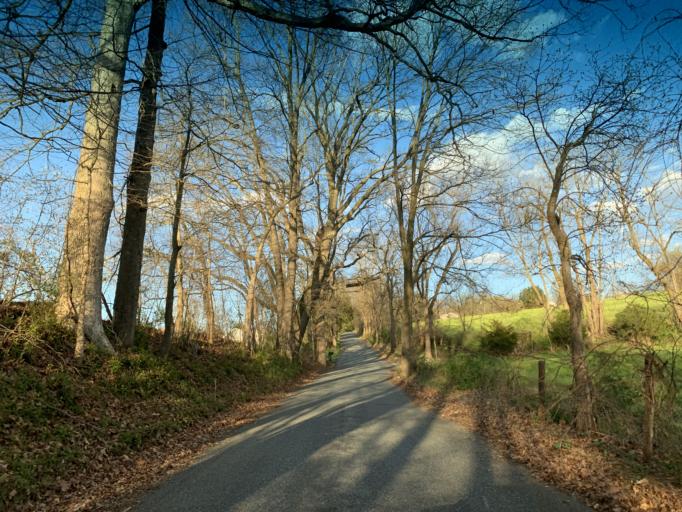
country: US
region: Maryland
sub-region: Harford County
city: South Bel Air
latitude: 39.6129
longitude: -76.3105
